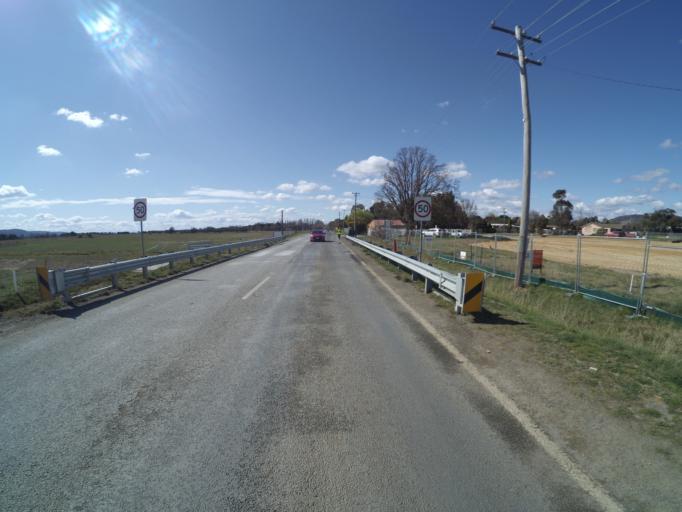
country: AU
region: New South Wales
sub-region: Palerang
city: Bungendore
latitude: -35.2618
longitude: 149.4349
